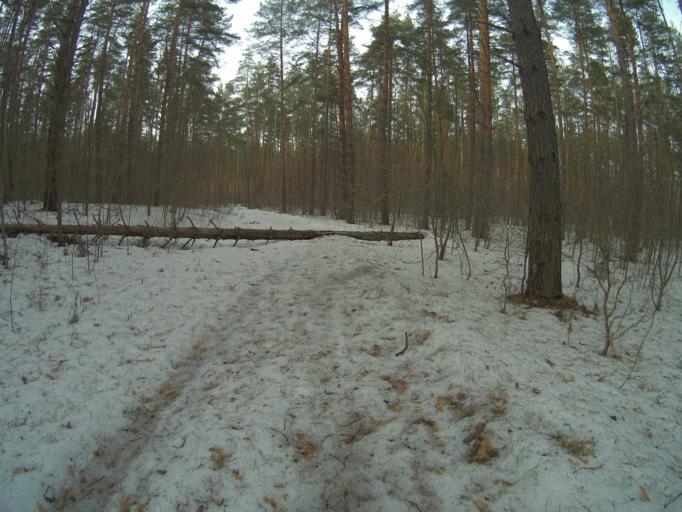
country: RU
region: Vladimir
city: Kommunar
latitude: 56.0702
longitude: 40.4417
